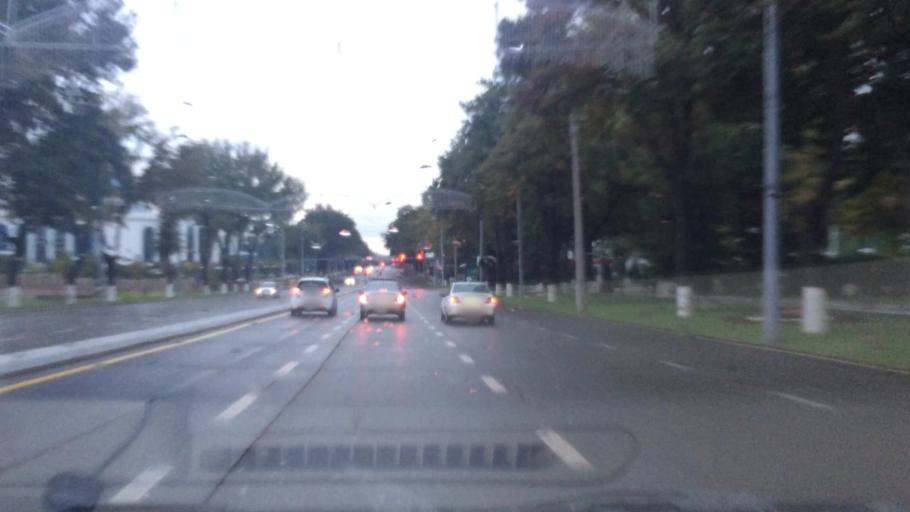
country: UZ
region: Toshkent Shahri
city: Tashkent
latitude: 41.3173
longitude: 69.2789
